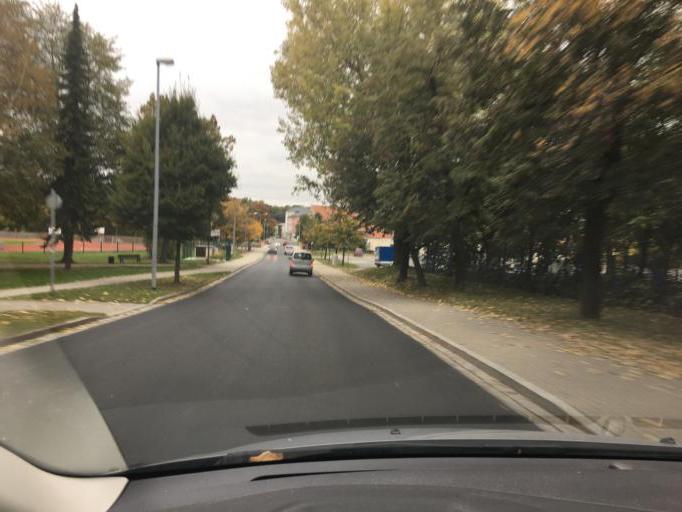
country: DE
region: Saxony
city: Freital
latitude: 51.0056
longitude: 13.6619
